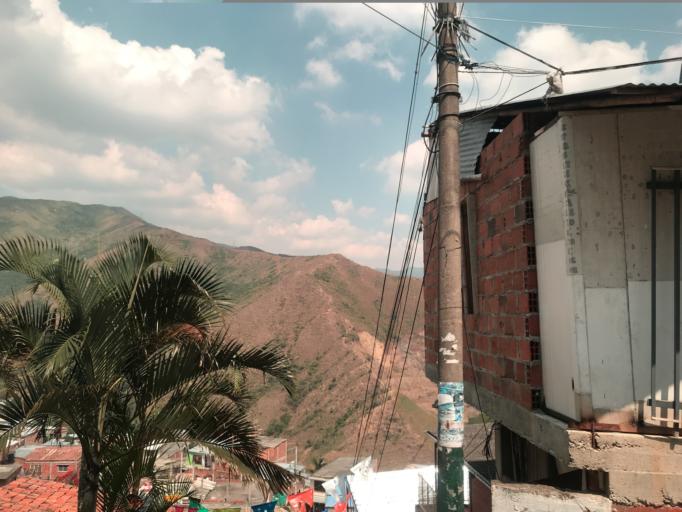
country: CO
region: Valle del Cauca
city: Cali
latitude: 3.4535
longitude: -76.5728
